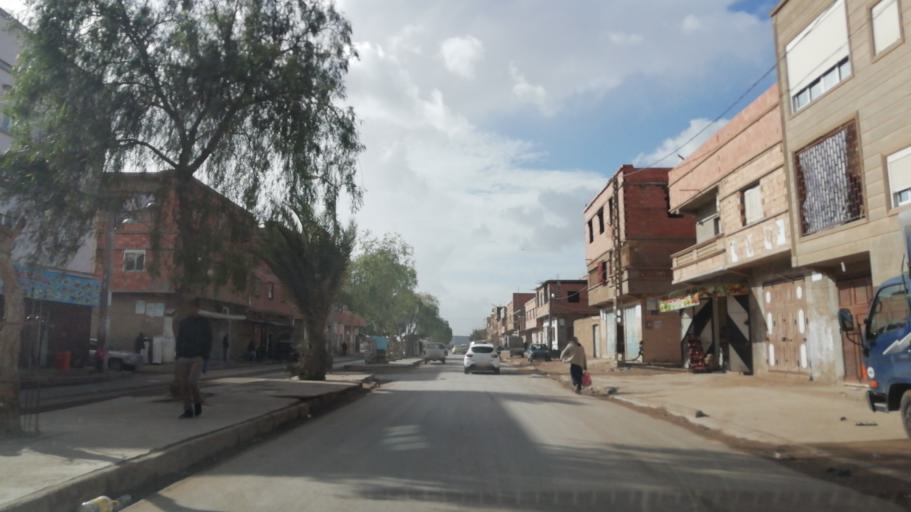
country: DZ
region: Oran
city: Es Senia
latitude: 35.6396
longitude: -0.5750
